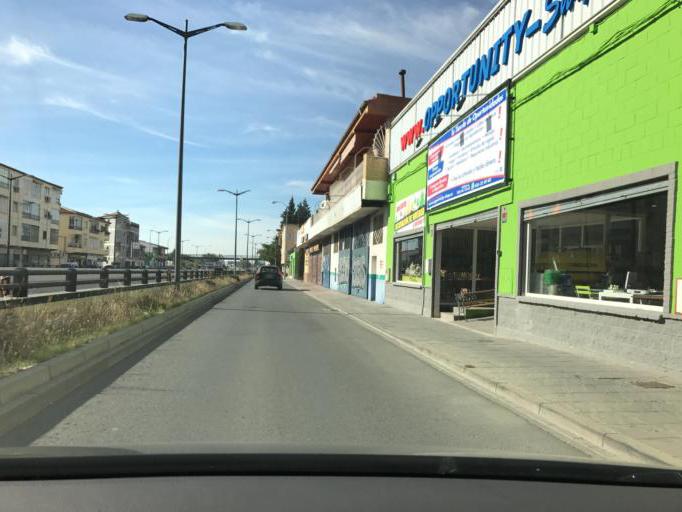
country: ES
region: Andalusia
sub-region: Provincia de Granada
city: Atarfe
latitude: 37.1926
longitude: -3.7153
